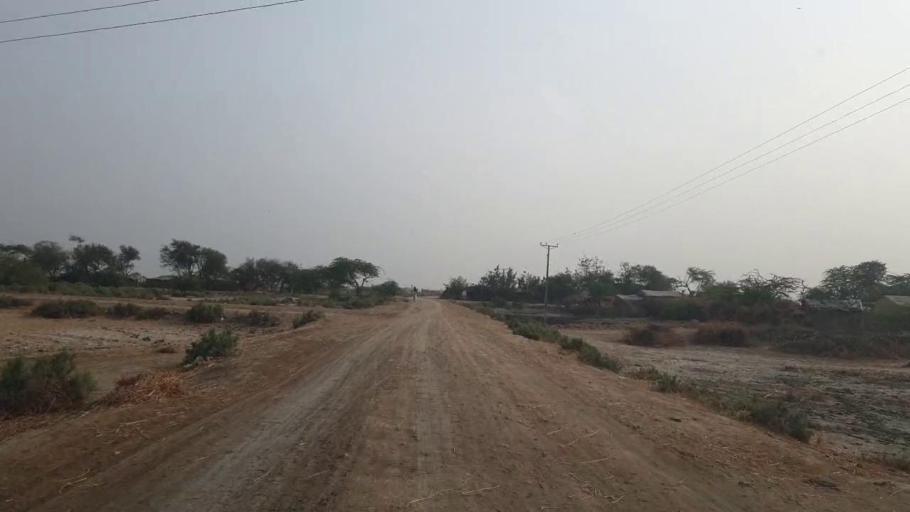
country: PK
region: Sindh
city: Mirpur Batoro
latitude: 24.5572
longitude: 68.4212
